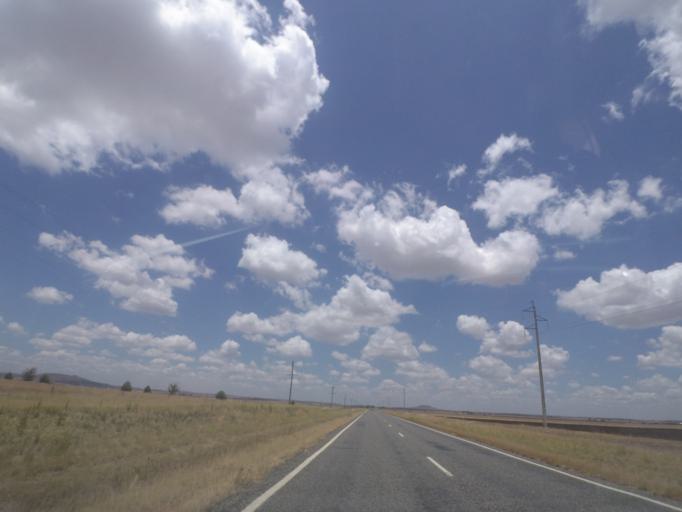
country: AU
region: Queensland
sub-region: Toowoomba
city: Top Camp
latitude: -27.9016
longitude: 151.9766
